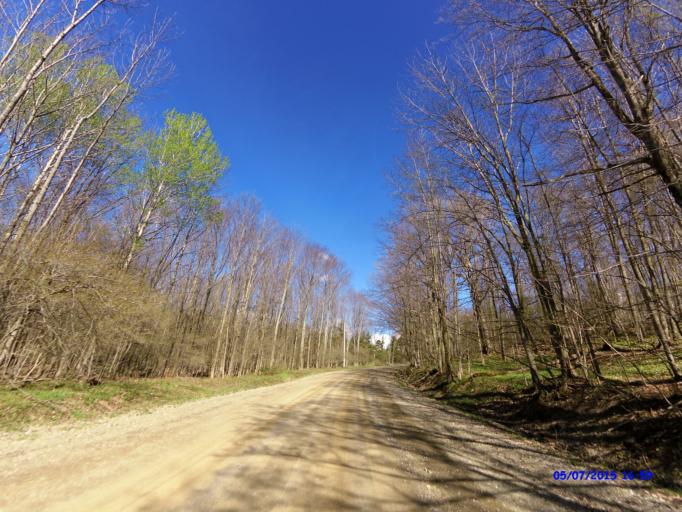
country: US
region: New York
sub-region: Cattaraugus County
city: Little Valley
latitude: 42.2897
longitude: -78.7381
